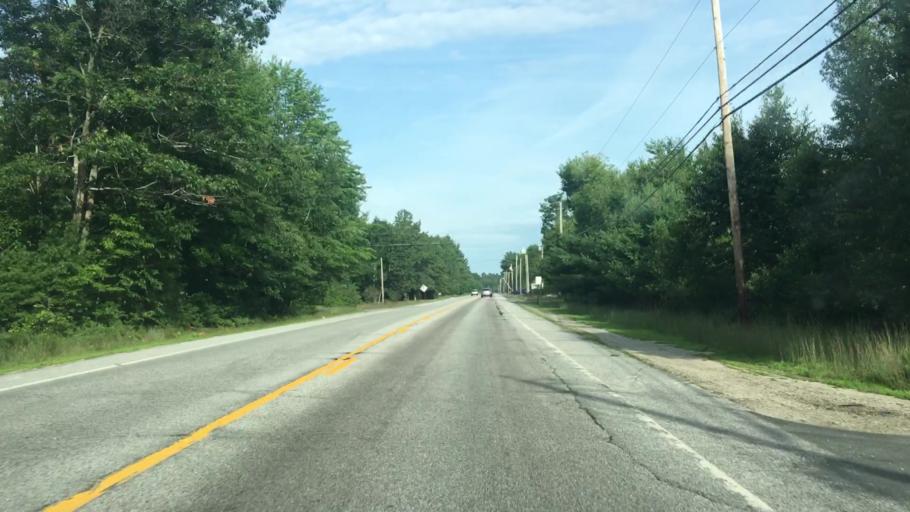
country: US
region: Maine
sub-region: Cumberland County
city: Steep Falls
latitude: 43.7333
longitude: -70.6160
